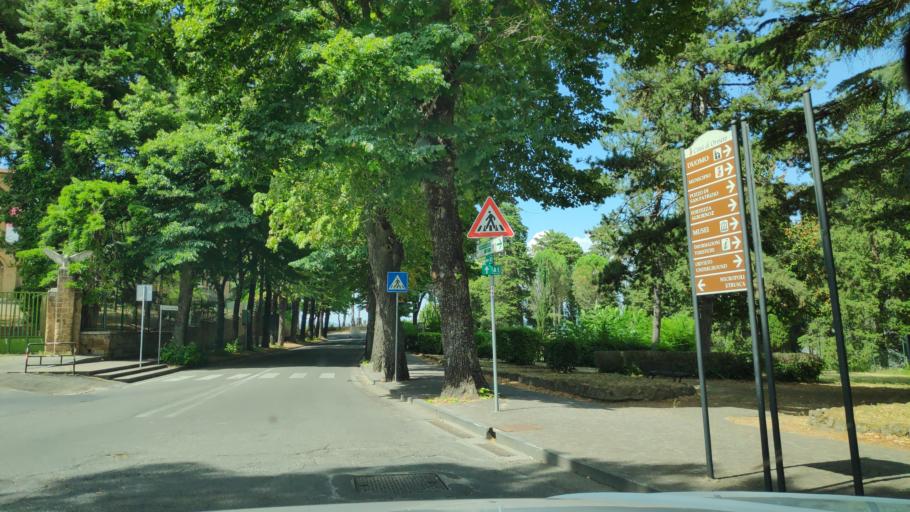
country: IT
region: Umbria
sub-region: Provincia di Terni
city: Orvieto
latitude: 42.7219
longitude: 12.1199
